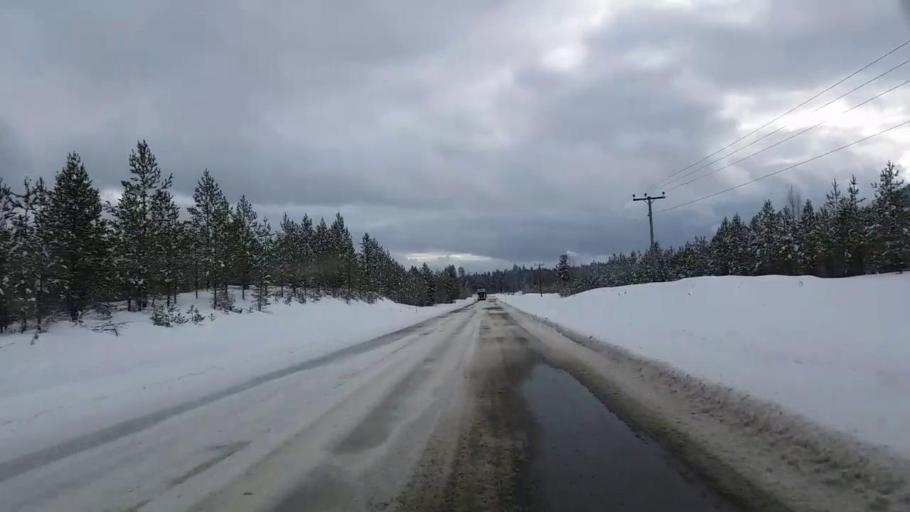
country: SE
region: Jaemtland
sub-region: Harjedalens Kommun
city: Sveg
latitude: 62.1072
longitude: 15.0644
